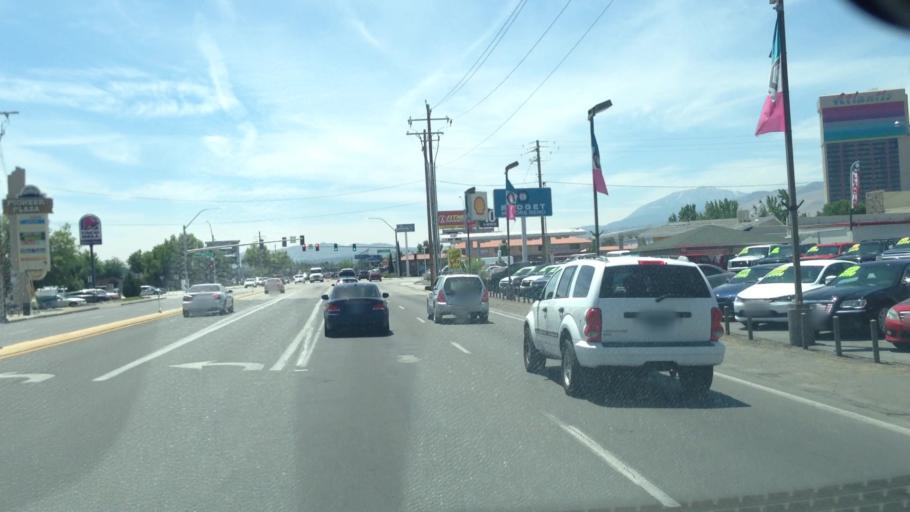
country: US
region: Nevada
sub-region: Washoe County
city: Reno
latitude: 39.4942
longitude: -119.7892
